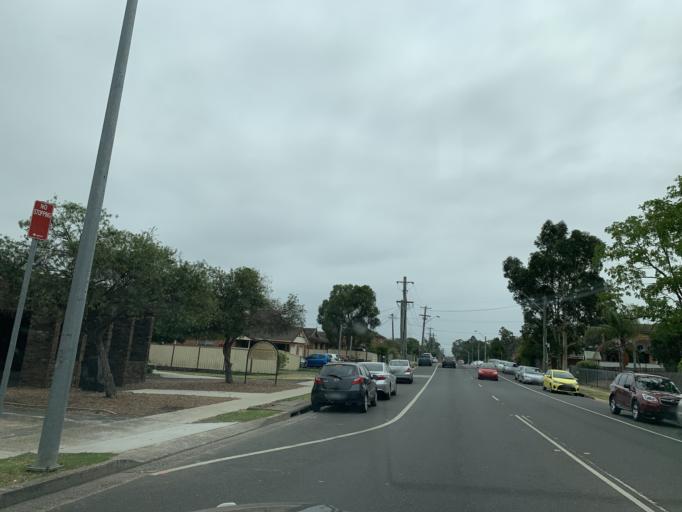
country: AU
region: New South Wales
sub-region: Blacktown
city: Doonside
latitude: -33.7621
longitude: 150.8696
